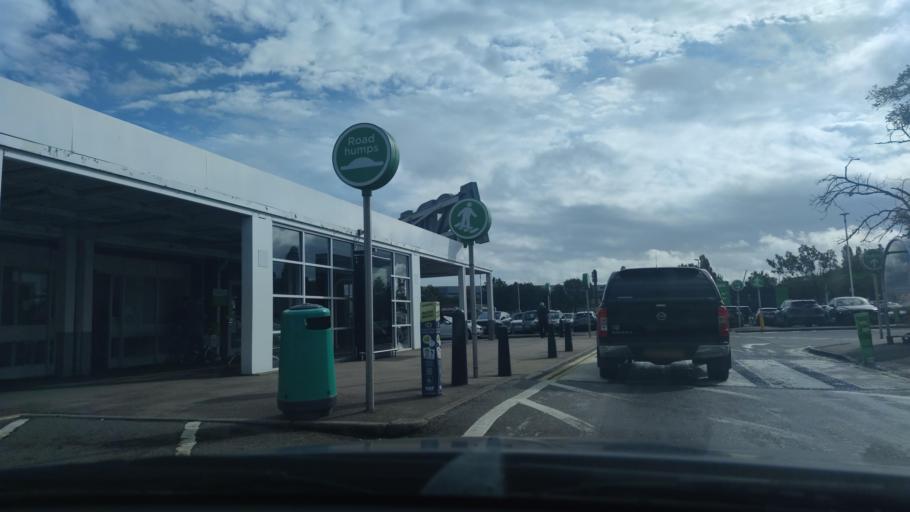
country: GB
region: England
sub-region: Borough of Thurrock
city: Tilbury
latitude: 51.4696
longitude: 0.3454
